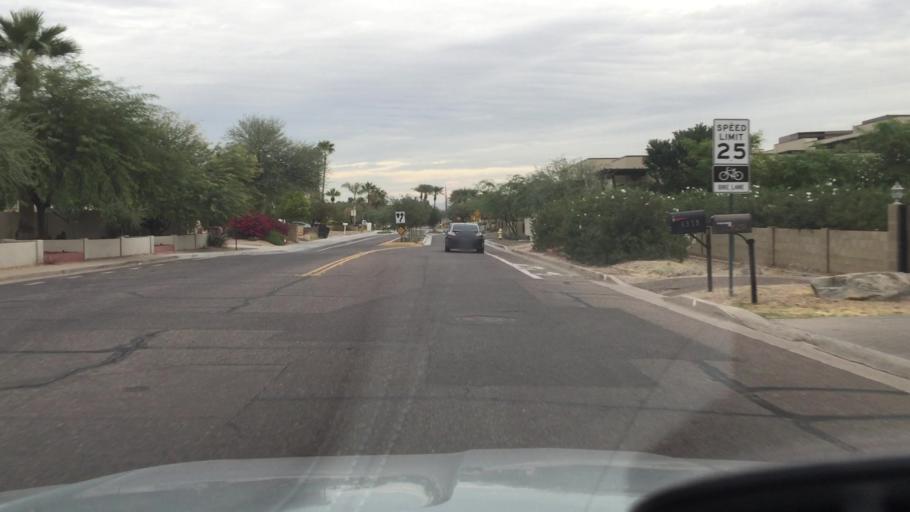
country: US
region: Arizona
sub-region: Maricopa County
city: Paradise Valley
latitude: 33.5095
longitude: -111.9309
